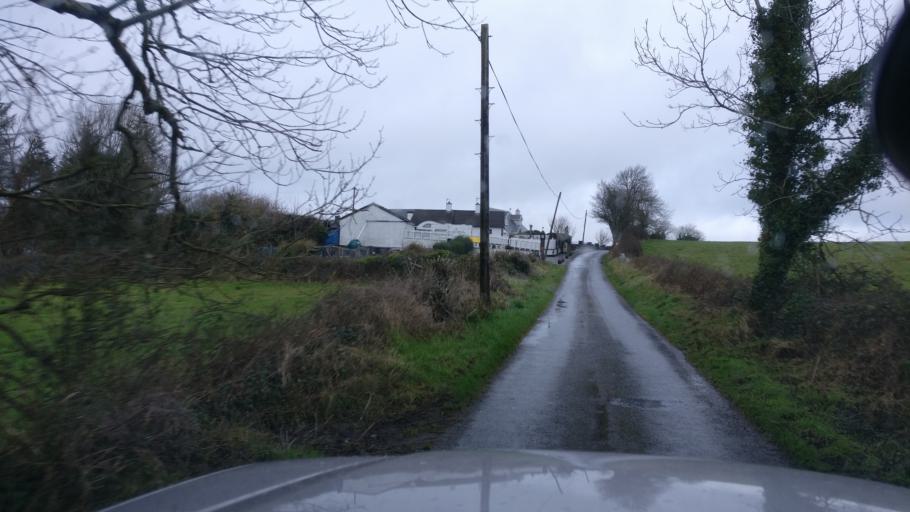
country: IE
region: Connaught
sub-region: County Galway
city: Loughrea
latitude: 53.1681
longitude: -8.6112
